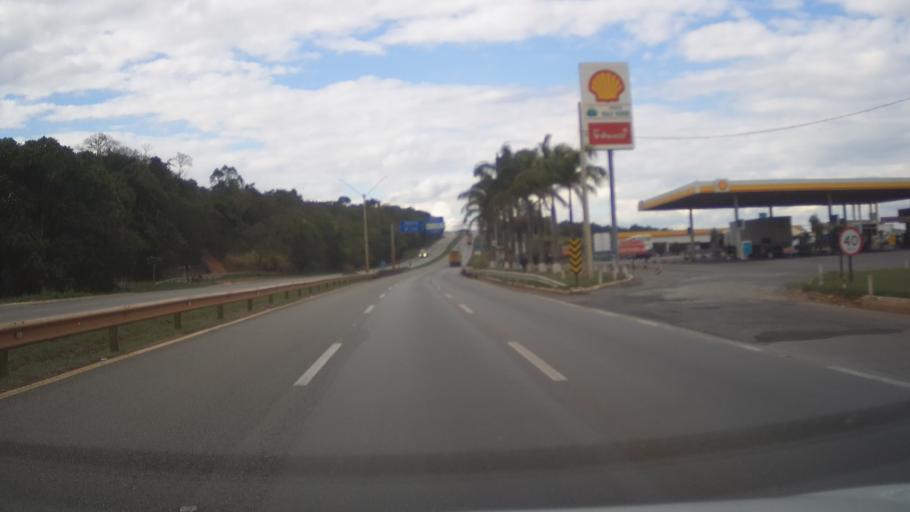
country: BR
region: Minas Gerais
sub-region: Igarape
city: Igarape
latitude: -20.2779
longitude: -44.4274
